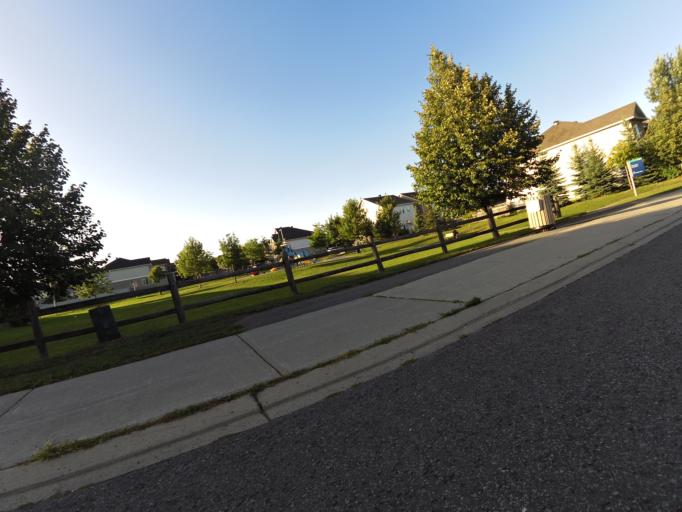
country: CA
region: Ontario
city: Bells Corners
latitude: 45.2747
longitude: -75.7424
